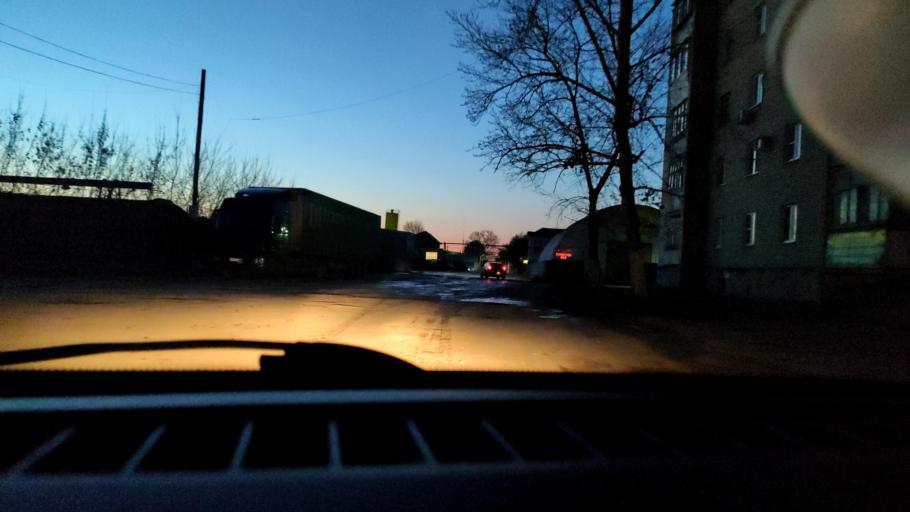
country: RU
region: Samara
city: Samara
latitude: 53.1285
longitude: 50.1081
